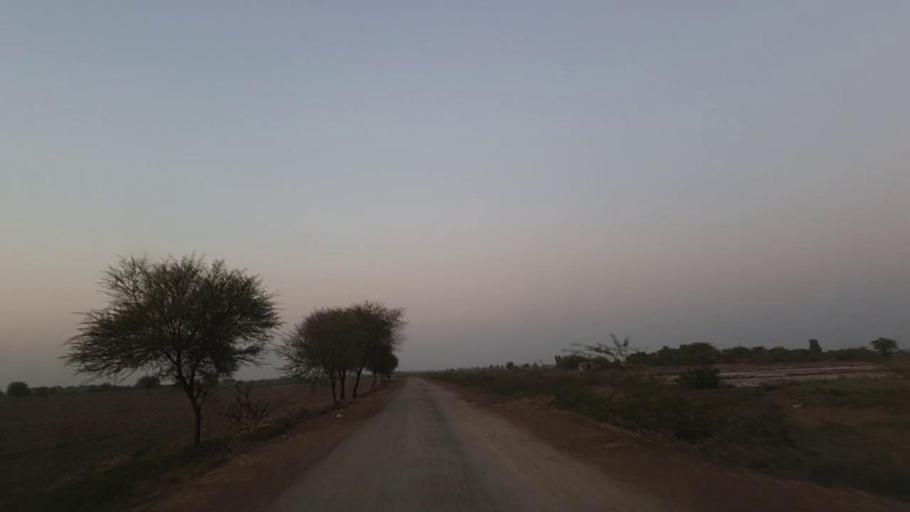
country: PK
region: Sindh
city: Naukot
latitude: 24.8769
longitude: 69.3903
